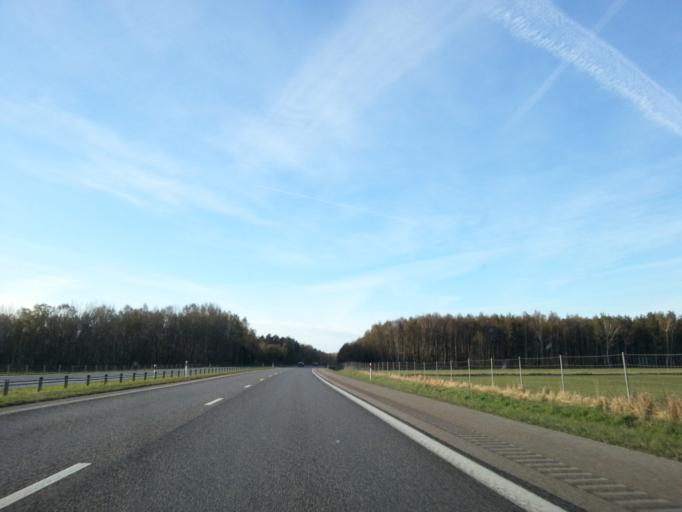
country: SE
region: Halland
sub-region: Laholms Kommun
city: Mellbystrand
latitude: 56.4624
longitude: 12.9426
